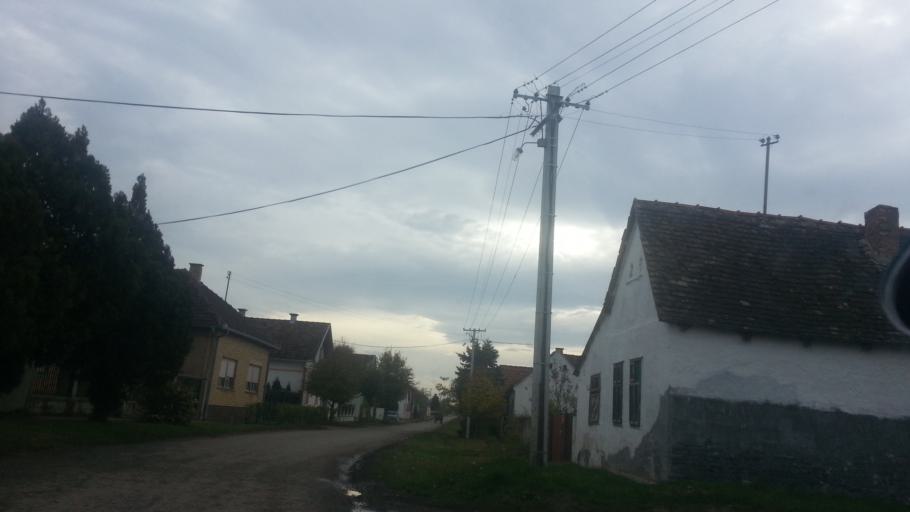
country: RS
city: Golubinci
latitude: 44.9878
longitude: 20.0587
